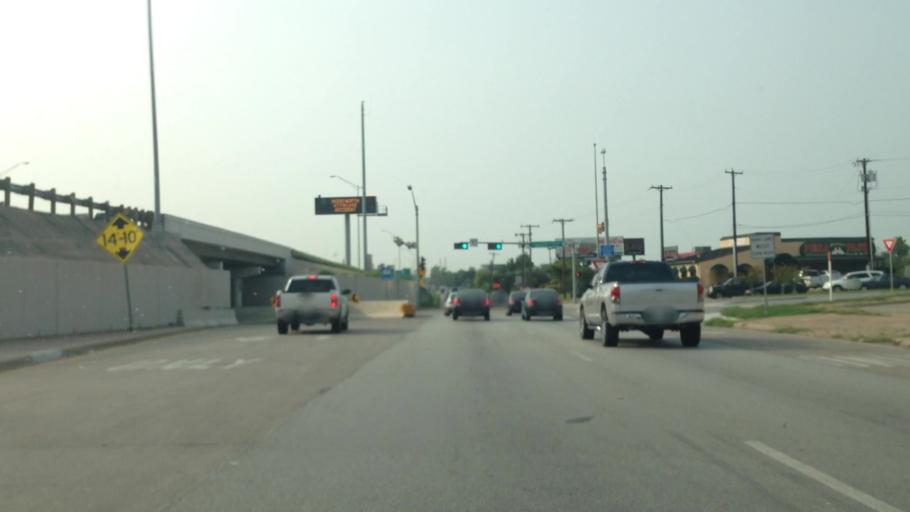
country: US
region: Texas
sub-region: Dallas County
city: Carrollton
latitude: 32.9679
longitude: -96.9188
